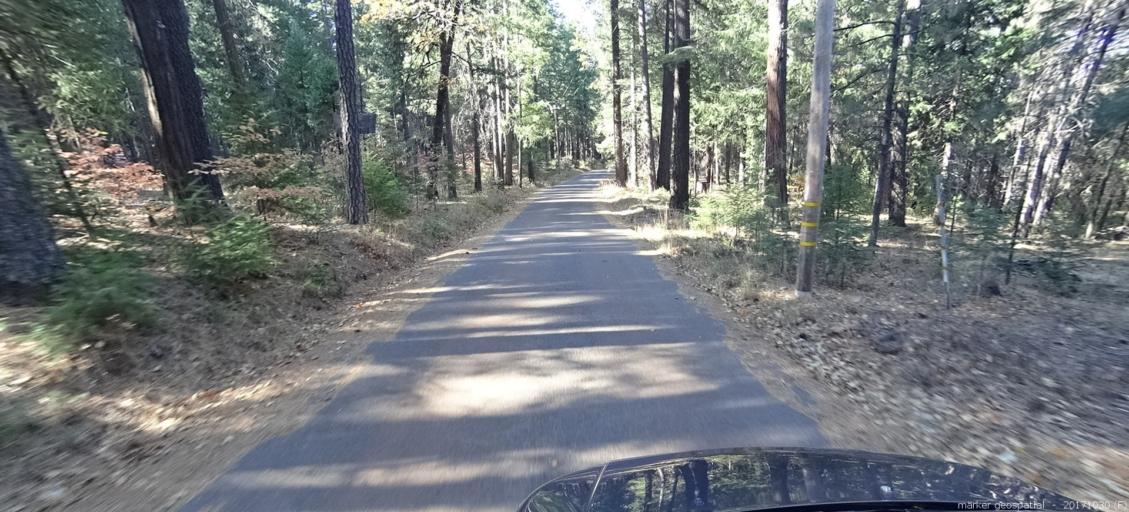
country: US
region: California
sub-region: Shasta County
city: Shingletown
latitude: 40.5186
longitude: -121.9021
